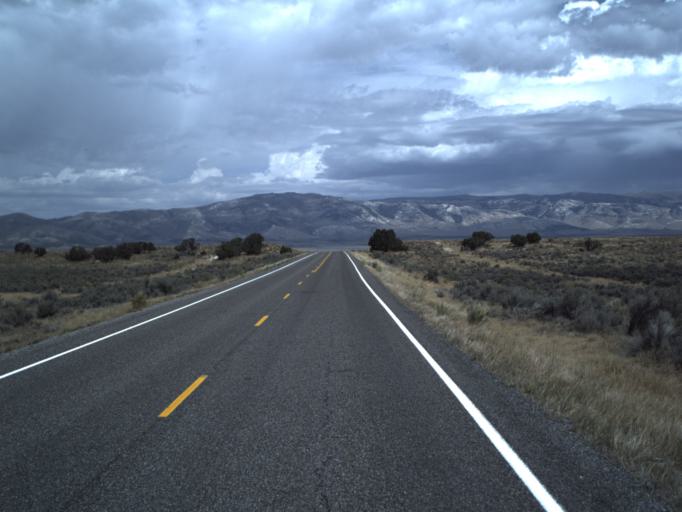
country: US
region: Idaho
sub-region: Cassia County
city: Burley
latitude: 41.7269
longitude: -113.5243
